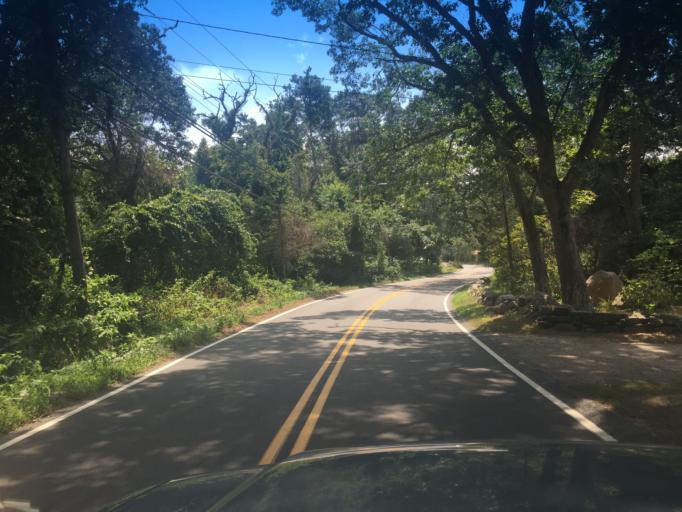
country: US
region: Massachusetts
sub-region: Barnstable County
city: West Falmouth
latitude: 41.5797
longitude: -70.6287
